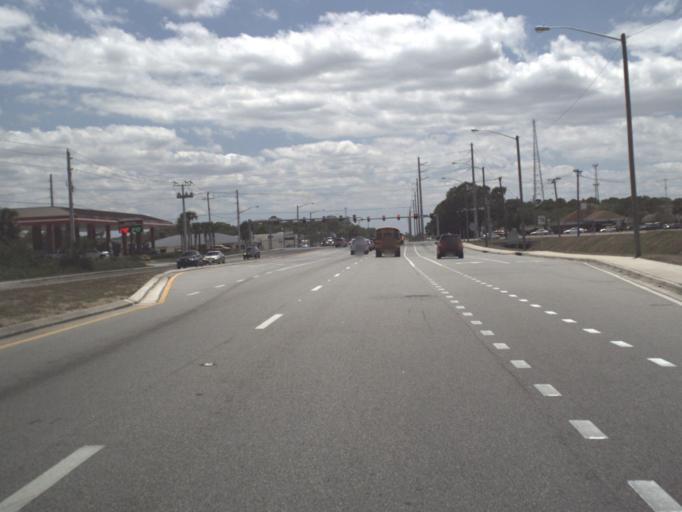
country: US
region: Florida
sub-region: Brevard County
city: Palm Bay
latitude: 28.0006
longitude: -80.6220
